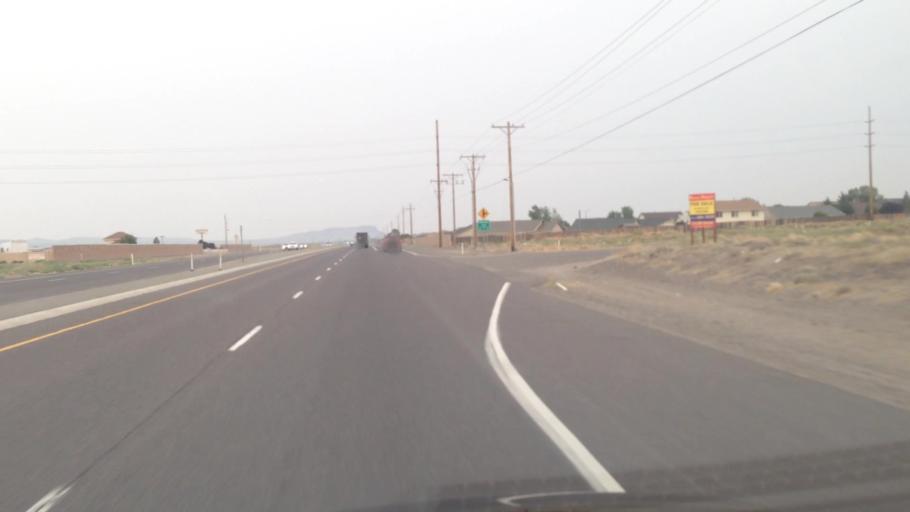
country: US
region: Nevada
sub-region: Lyon County
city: Fernley
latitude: 39.6000
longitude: -119.2104
